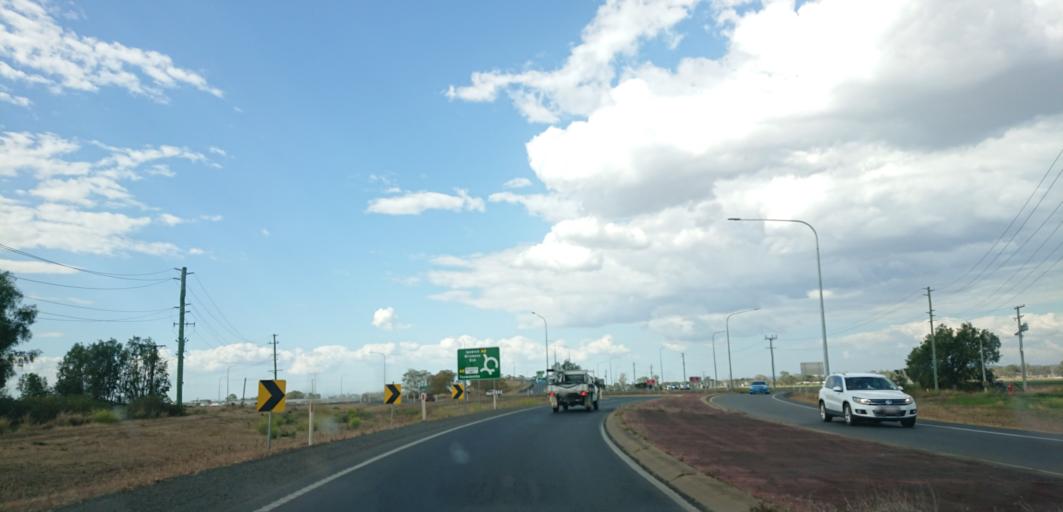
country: AU
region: Queensland
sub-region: Lockyer Valley
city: Gatton
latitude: -27.5502
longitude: 152.3137
